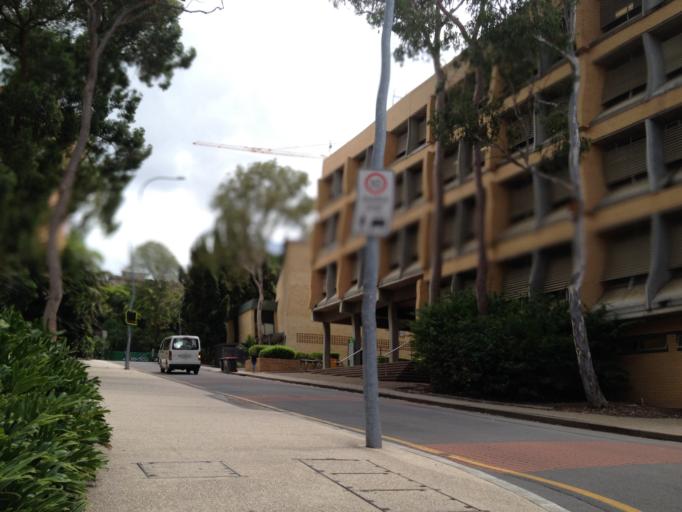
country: AU
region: Queensland
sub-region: Brisbane
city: Yeronga
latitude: -27.4998
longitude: 153.0131
